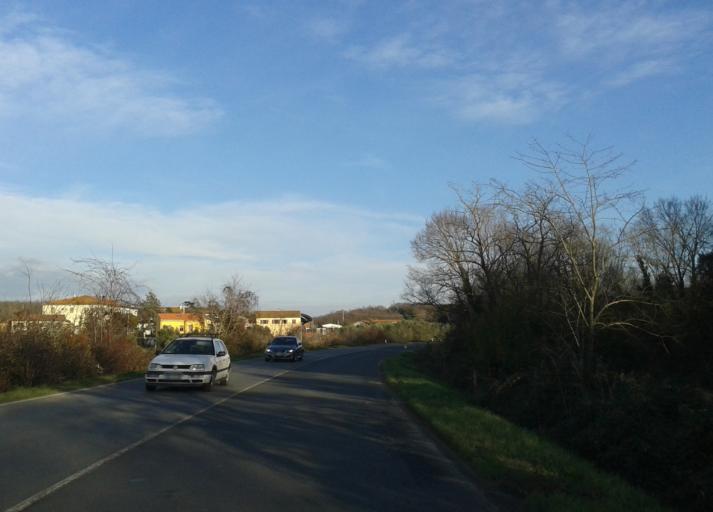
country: IT
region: Tuscany
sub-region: Provincia di Livorno
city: Guasticce
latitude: 43.5729
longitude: 10.3714
